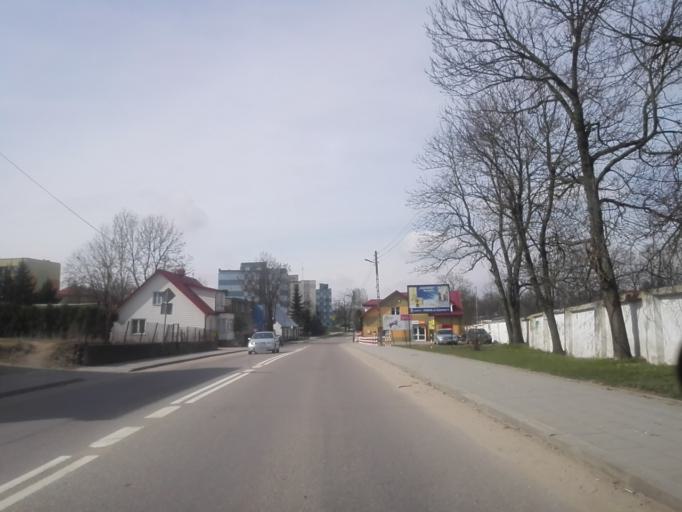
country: PL
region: Podlasie
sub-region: Powiat sejnenski
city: Sejny
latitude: 54.1078
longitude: 23.3451
